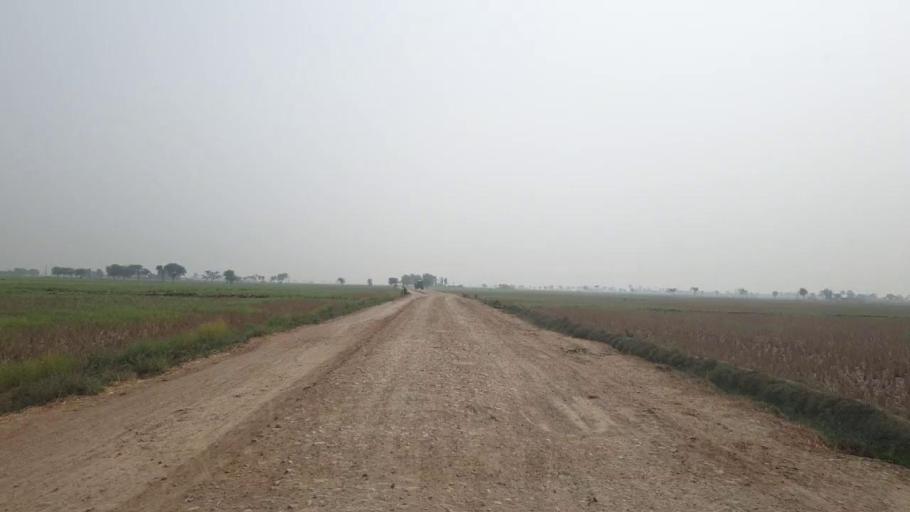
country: PK
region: Sindh
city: Kario
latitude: 24.6464
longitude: 68.5953
